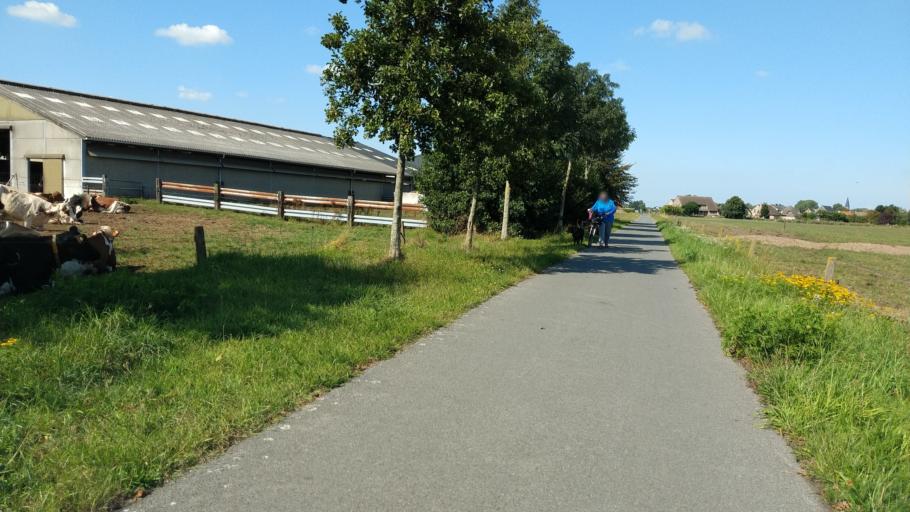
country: BE
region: Flanders
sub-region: Provincie Oost-Vlaanderen
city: Assenede
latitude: 51.2180
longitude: 3.7690
